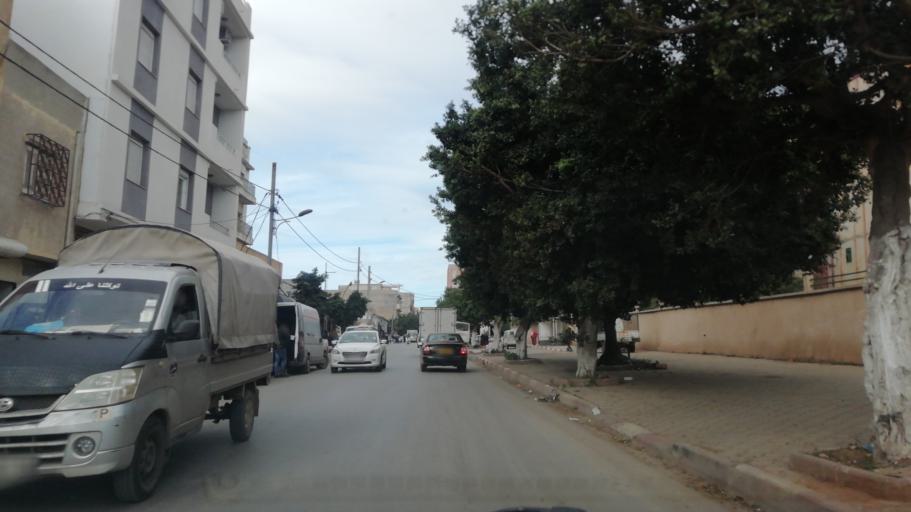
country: DZ
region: Oran
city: Oran
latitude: 35.6838
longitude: -0.6138
